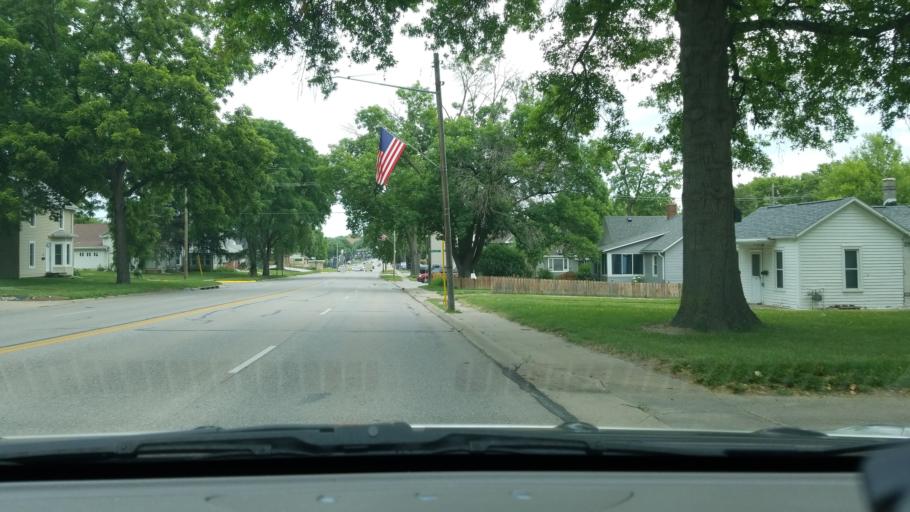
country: US
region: Nebraska
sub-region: Sarpy County
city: Papillion
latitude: 41.1500
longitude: -96.0429
